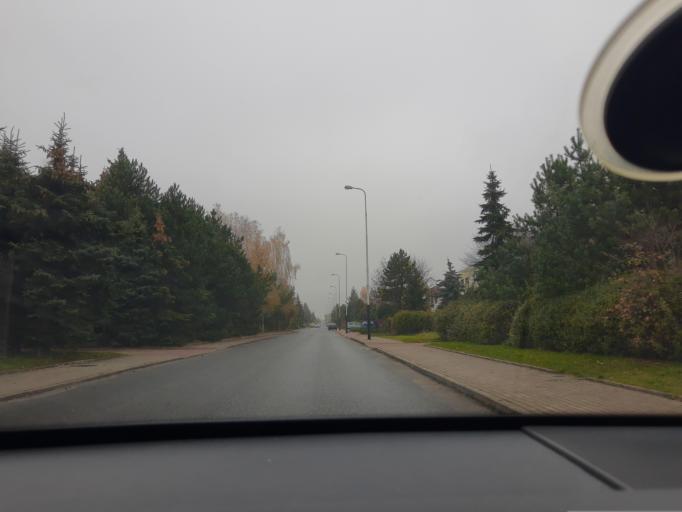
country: PL
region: Lodz Voivodeship
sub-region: Powiat pabianicki
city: Konstantynow Lodzki
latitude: 51.7364
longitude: 19.3807
